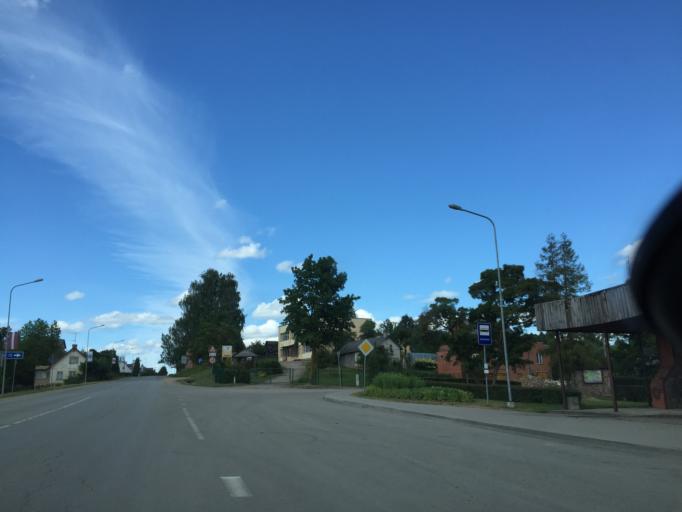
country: LT
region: Panevezys
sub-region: Birzai
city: Birzai
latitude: 56.3795
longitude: 24.6447
